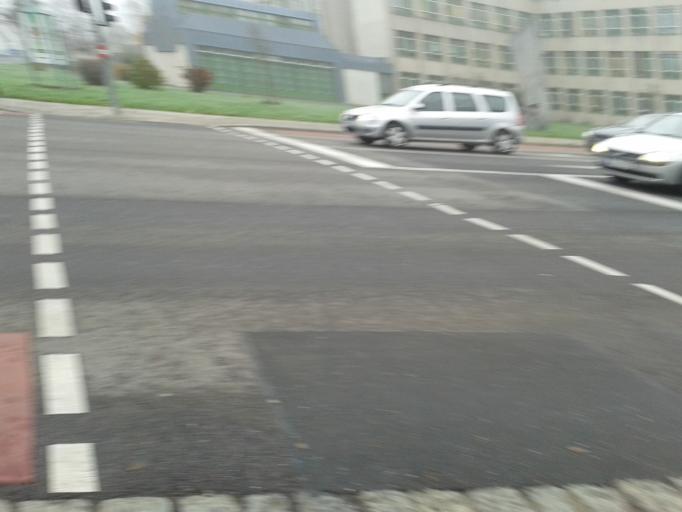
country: DE
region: Bavaria
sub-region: Upper Franconia
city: Bamberg
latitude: 49.8988
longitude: 10.9086
